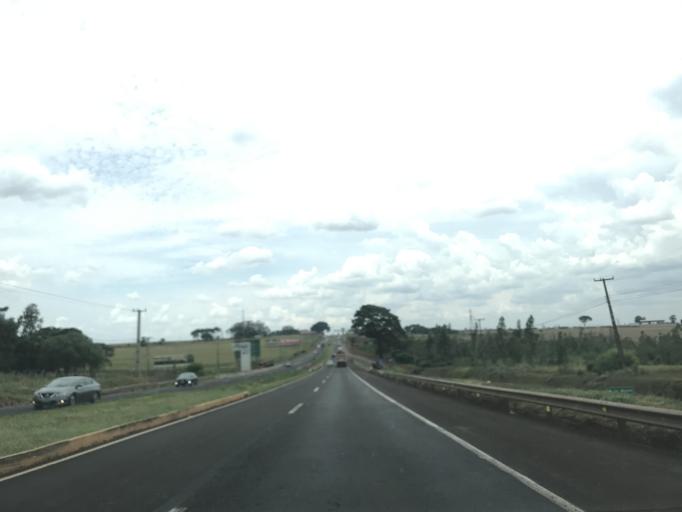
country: BR
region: Parana
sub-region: Paicandu
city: Paicandu
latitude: -23.3936
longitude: -52.0096
